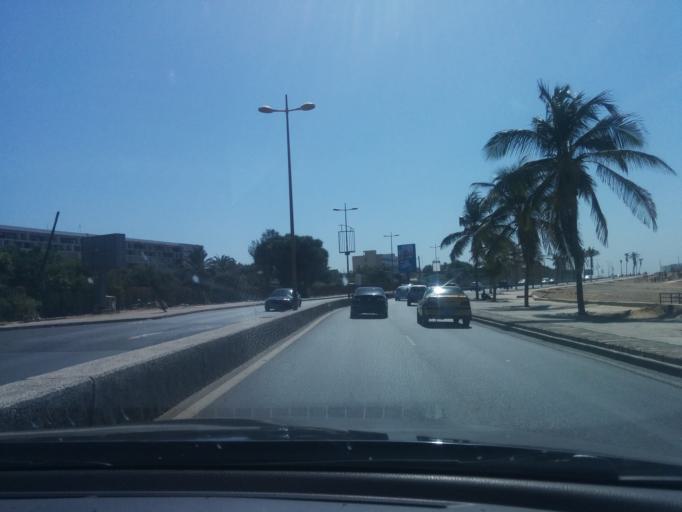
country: SN
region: Dakar
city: Mermoz Boabab
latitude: 14.6842
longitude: -17.4686
